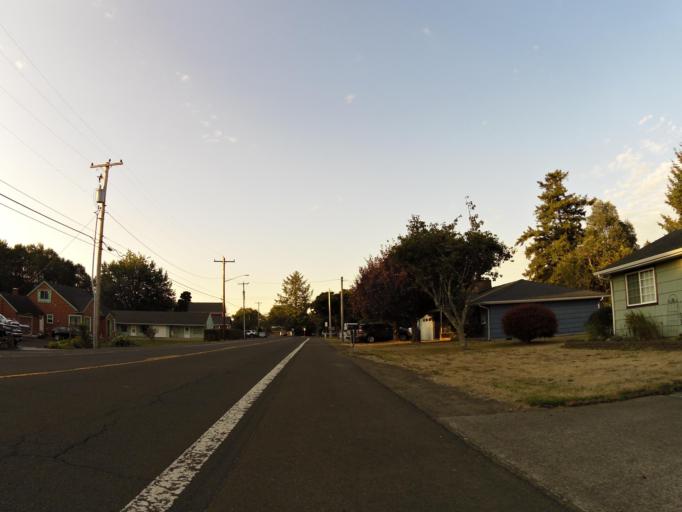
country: US
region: Oregon
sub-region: Clatsop County
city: Warrenton
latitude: 46.1541
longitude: -123.9277
